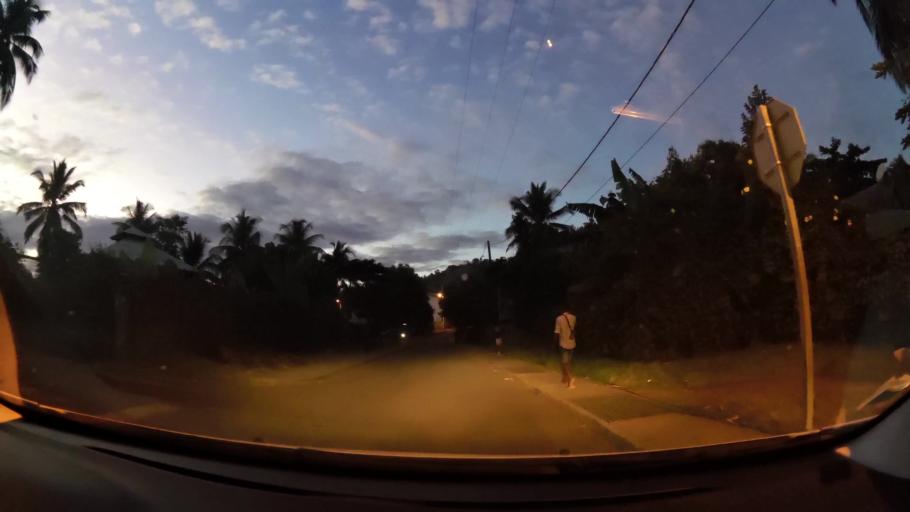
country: YT
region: Bandraboua
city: Bandraboua
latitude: -12.7210
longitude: 45.1190
